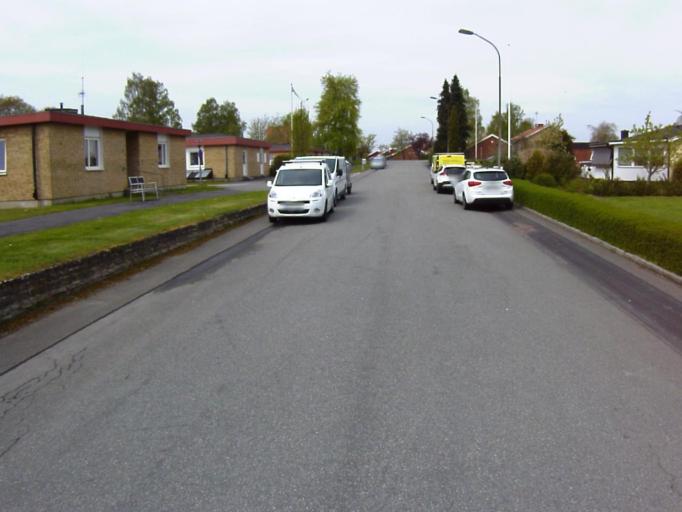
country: SE
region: Skane
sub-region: Kristianstads Kommun
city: Onnestad
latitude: 55.9330
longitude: 13.9890
